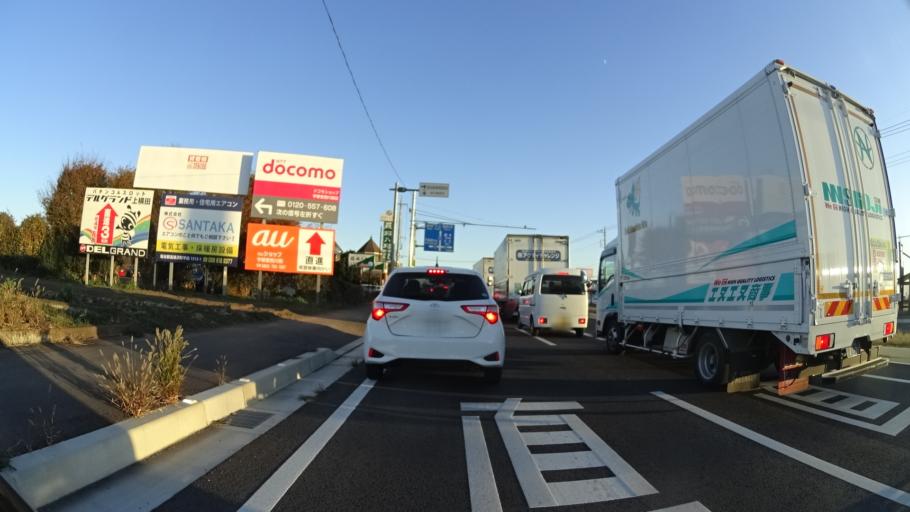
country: JP
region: Tochigi
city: Utsunomiya-shi
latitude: 36.5174
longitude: 139.8422
